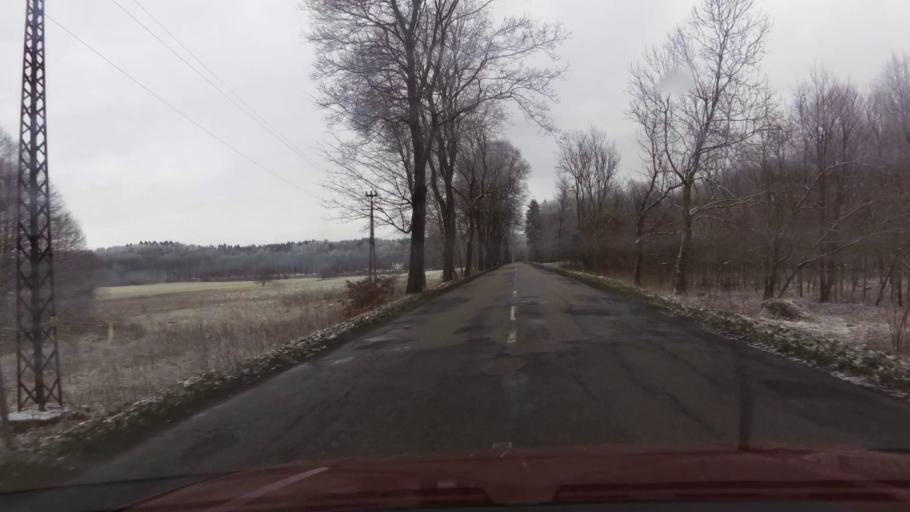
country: PL
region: West Pomeranian Voivodeship
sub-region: Powiat swidwinski
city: Polczyn-Zdroj
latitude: 53.7926
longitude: 16.0506
